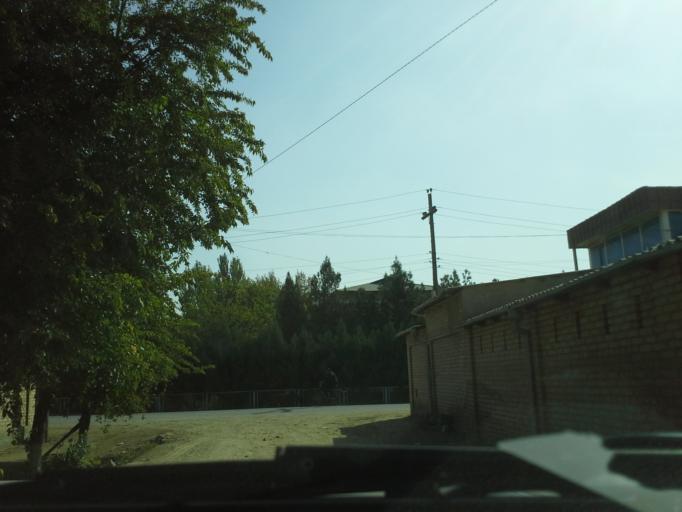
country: TM
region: Lebap
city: Atamyrat
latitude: 37.8470
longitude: 65.1925
